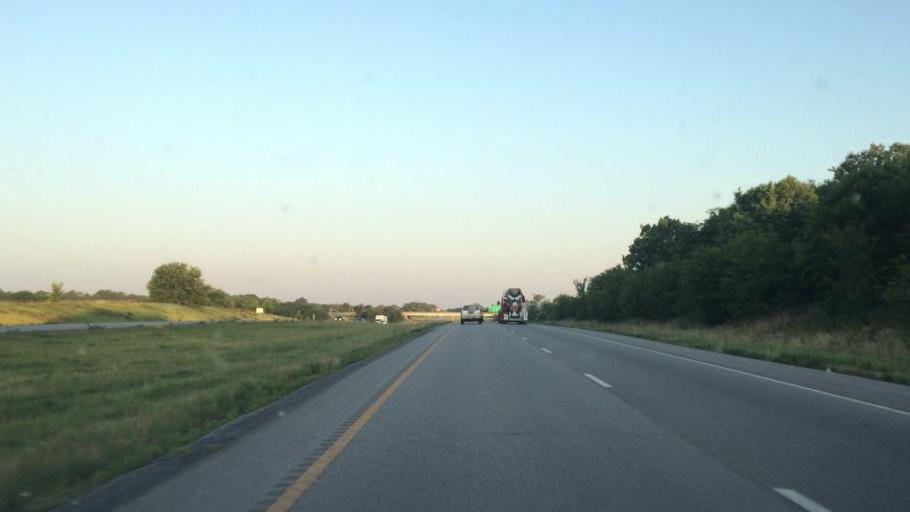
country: US
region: Missouri
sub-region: Clay County
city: Smithville
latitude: 39.3113
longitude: -94.5483
